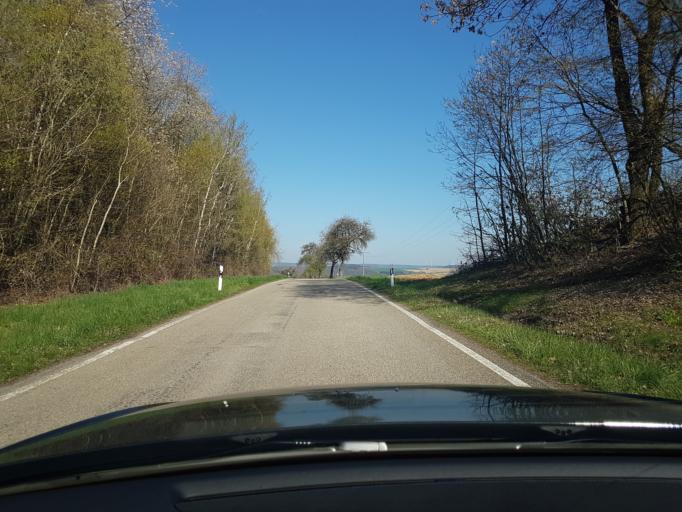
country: DE
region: Baden-Wuerttemberg
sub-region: Regierungsbezirk Stuttgart
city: Jagsthausen
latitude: 49.3159
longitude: 9.5155
